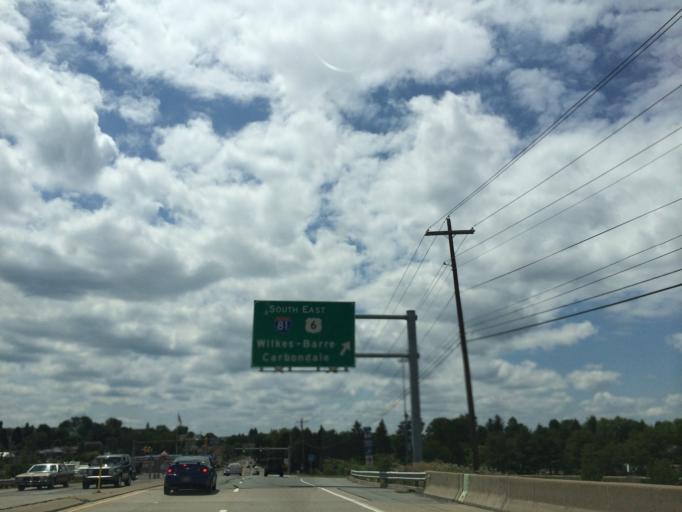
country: US
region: Pennsylvania
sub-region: Lackawanna County
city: Dunmore
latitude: 41.4309
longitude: -75.6226
